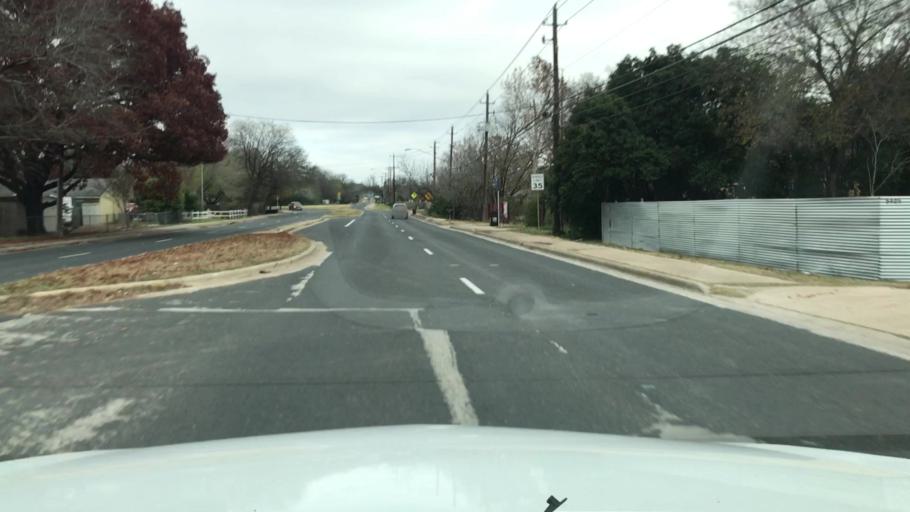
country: US
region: Texas
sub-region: Travis County
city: Onion Creek
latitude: 30.1824
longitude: -97.7457
